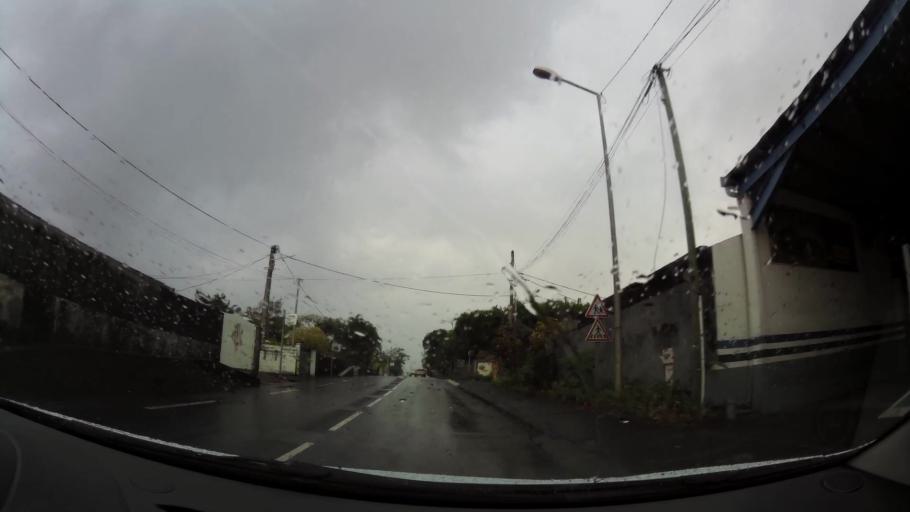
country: RE
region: Reunion
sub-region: Reunion
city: Saint-Benoit
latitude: -21.0291
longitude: 55.7081
